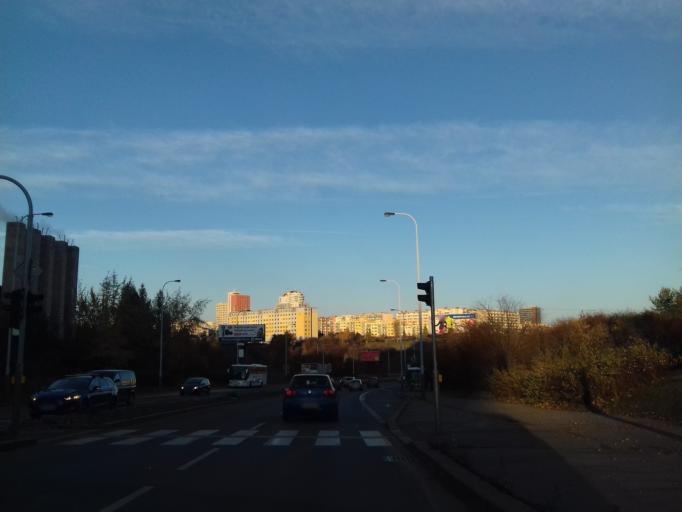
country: CZ
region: Praha
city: Branik
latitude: 50.0441
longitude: 14.3380
